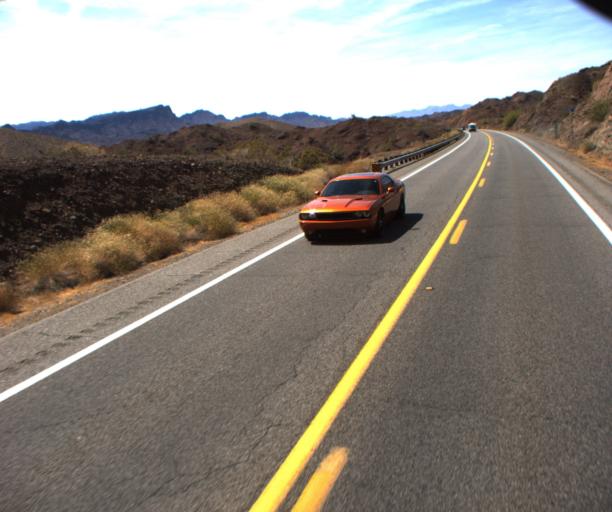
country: US
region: Arizona
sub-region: La Paz County
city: Cienega Springs
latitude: 34.3207
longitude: -114.1180
